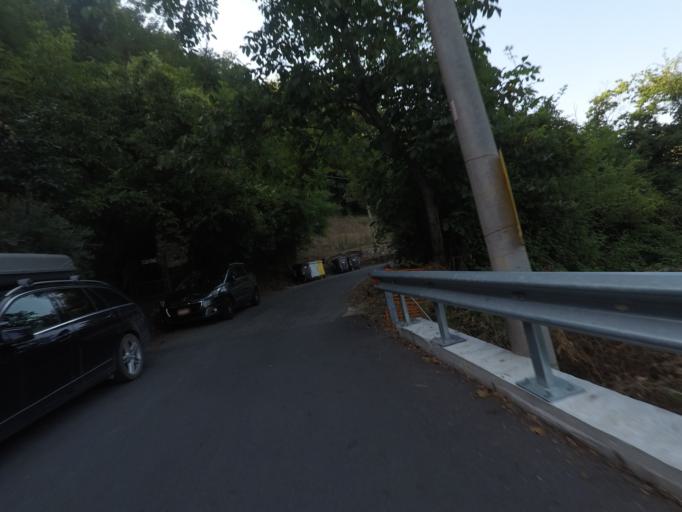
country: IT
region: Tuscany
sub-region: Provincia di Massa-Carrara
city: Carrara
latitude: 44.0763
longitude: 10.0660
